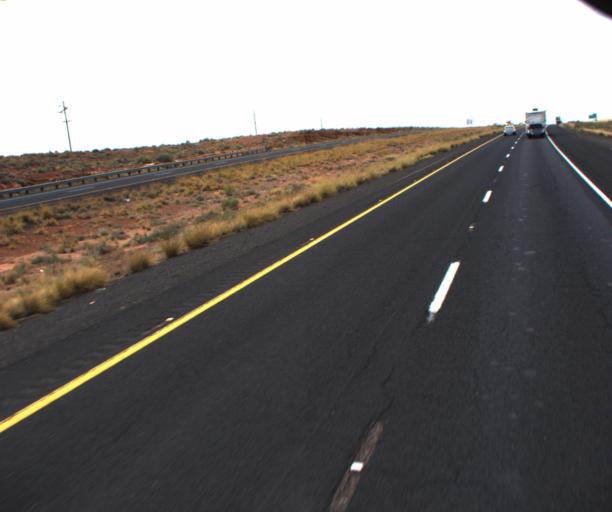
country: US
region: Arizona
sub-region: Navajo County
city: Holbrook
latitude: 34.9101
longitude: -110.2341
